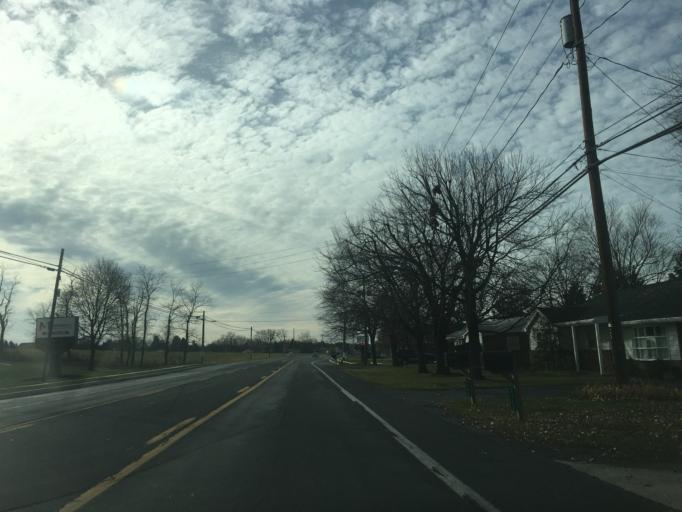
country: US
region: Pennsylvania
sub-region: Dauphin County
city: Progress
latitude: 40.3309
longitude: -76.8528
